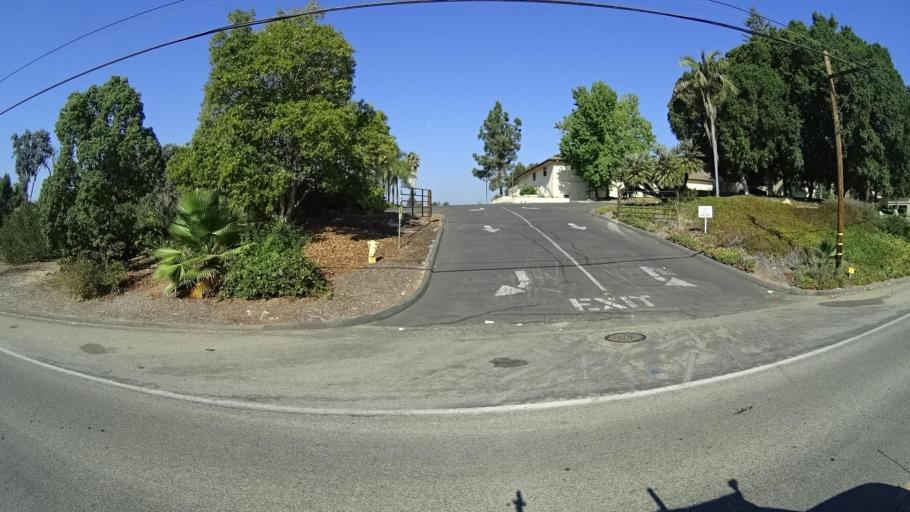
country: US
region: California
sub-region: San Diego County
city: Fallbrook
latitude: 33.3733
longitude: -117.2277
